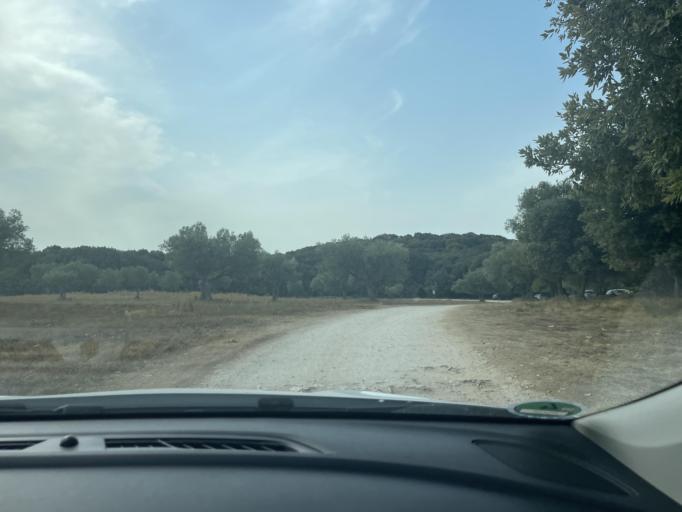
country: HR
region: Istarska
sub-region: Grad Rovinj
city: Rovinj
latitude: 45.0378
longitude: 13.6920
